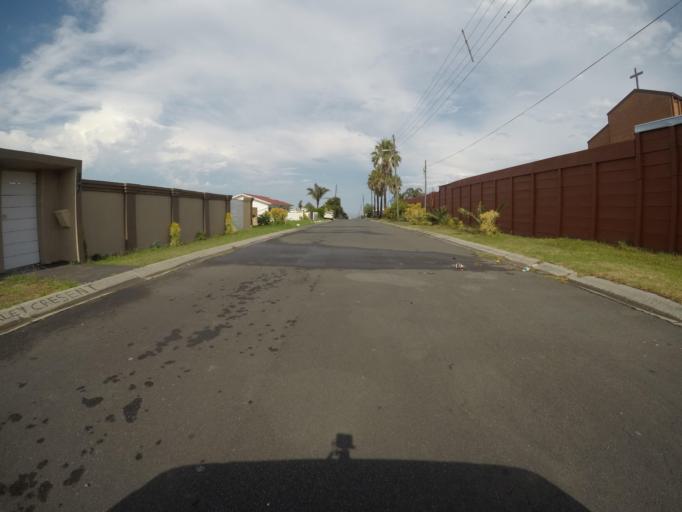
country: ZA
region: Eastern Cape
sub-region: Buffalo City Metropolitan Municipality
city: East London
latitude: -33.0216
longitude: 27.8726
